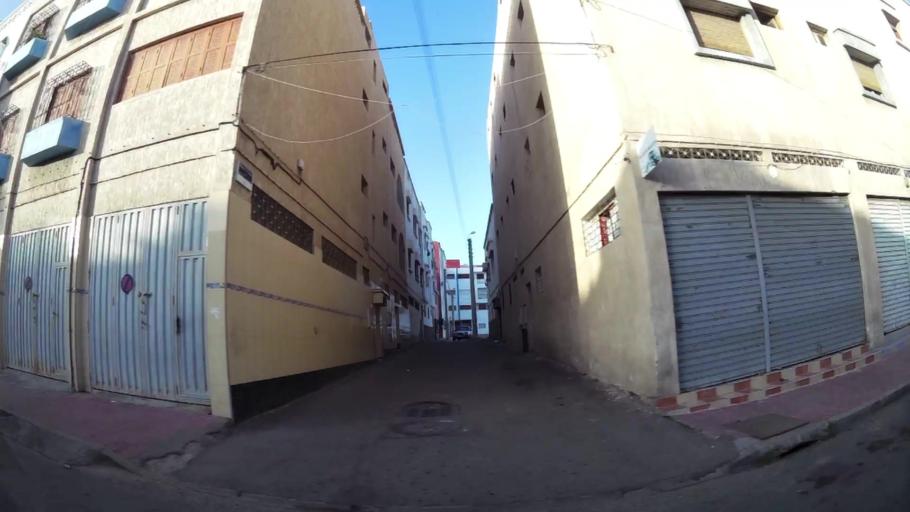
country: MA
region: Oued ed Dahab-Lagouira
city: Dakhla
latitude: 30.4134
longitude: -9.5582
